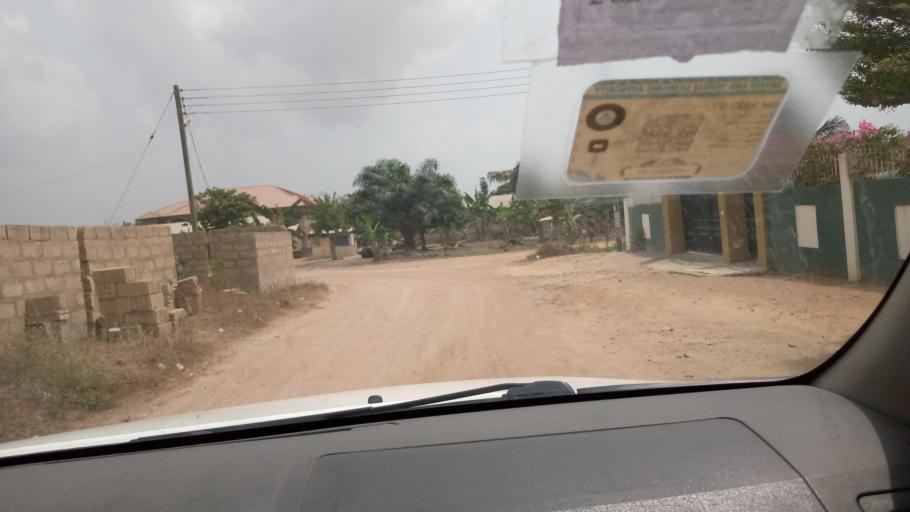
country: GH
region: Central
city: Kasoa
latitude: 5.5338
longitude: -0.4503
